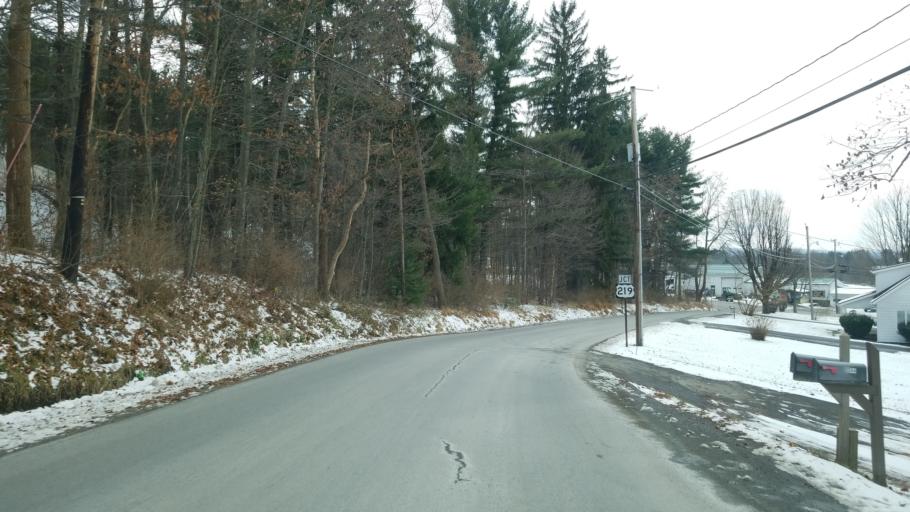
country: US
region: Pennsylvania
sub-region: Clearfield County
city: Sandy
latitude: 41.0772
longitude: -78.7500
